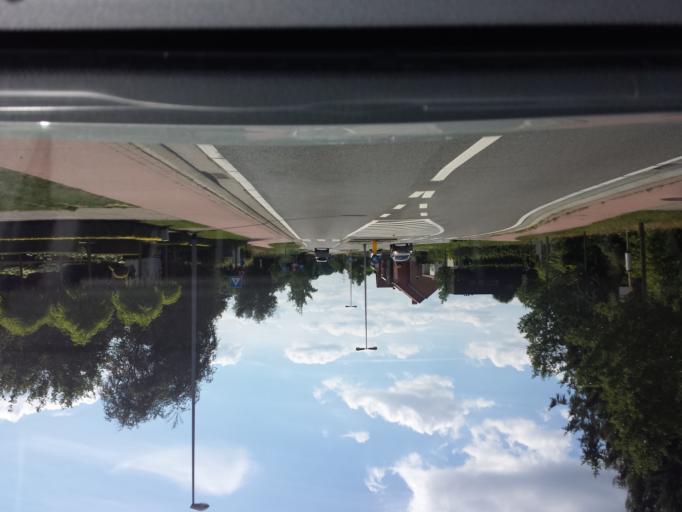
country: BE
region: Flanders
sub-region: Provincie Limburg
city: Beringen
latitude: 51.0310
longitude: 5.2107
